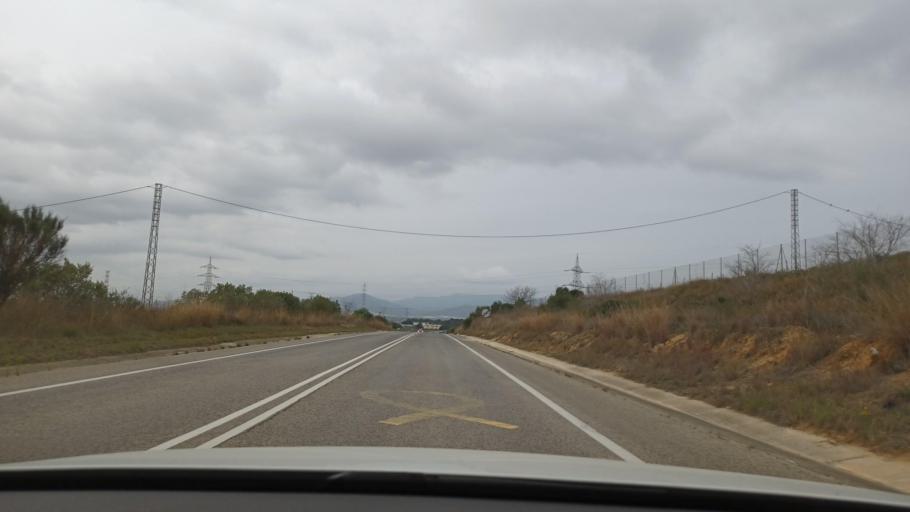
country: ES
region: Catalonia
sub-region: Provincia de Tarragona
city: La Secuita
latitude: 41.1972
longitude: 1.2575
